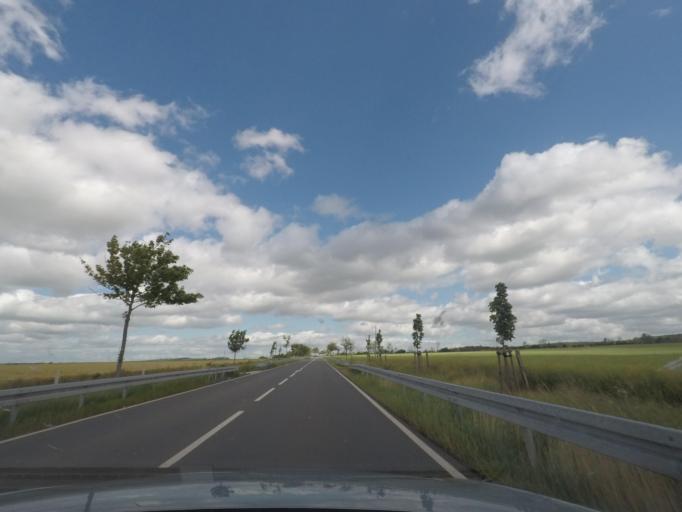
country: DE
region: Saxony-Anhalt
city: Harsleben
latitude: 51.8366
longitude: 11.1117
